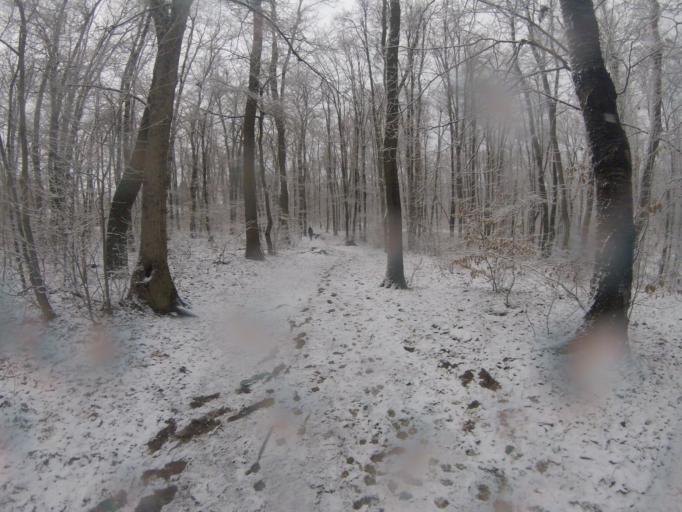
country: HU
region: Pest
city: Pilisszentivan
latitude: 47.5854
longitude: 18.9053
